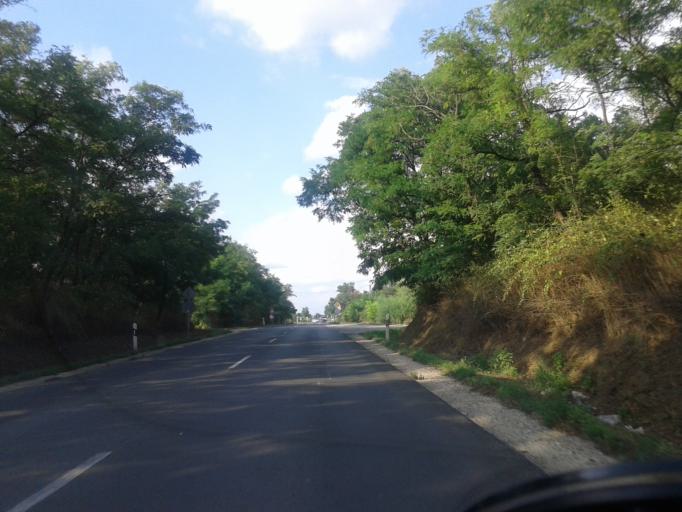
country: HU
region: Pest
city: Kiskunlachaza
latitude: 47.2125
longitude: 19.0165
